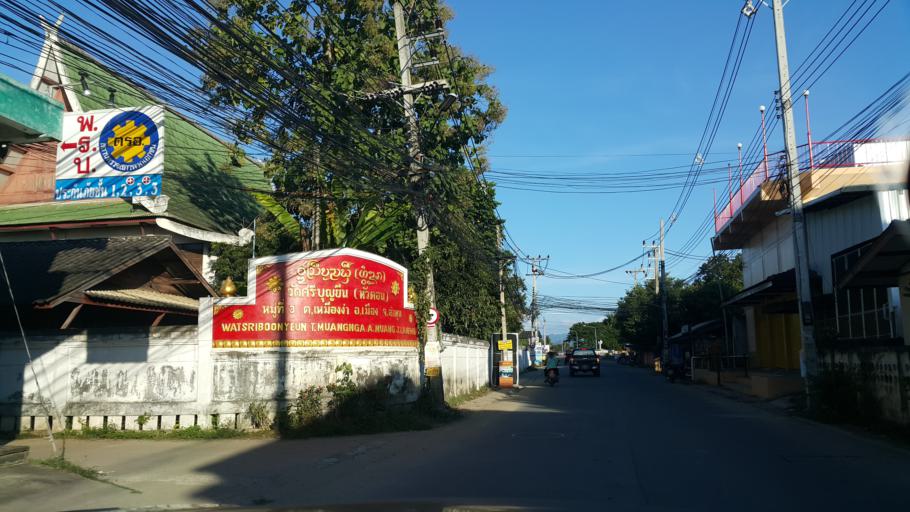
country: TH
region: Lamphun
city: Lamphun
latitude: 18.5993
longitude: 99.0292
